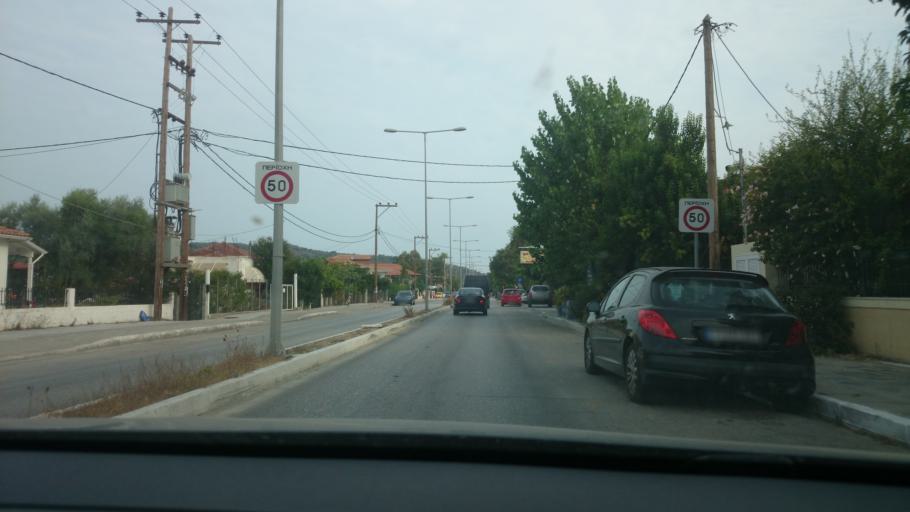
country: GR
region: Ionian Islands
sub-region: Lefkada
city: Lefkada
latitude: 38.7939
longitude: 20.7179
